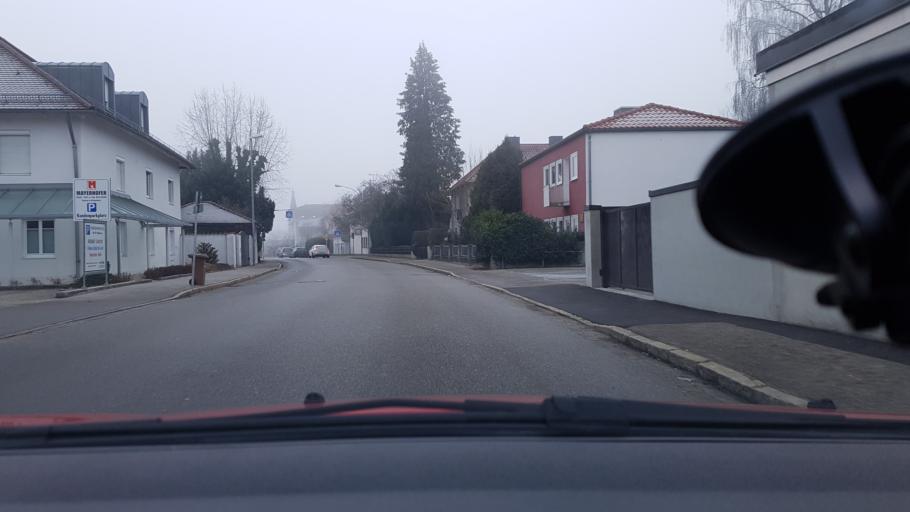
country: DE
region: Bavaria
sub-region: Lower Bavaria
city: Simbach am Inn
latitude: 48.2673
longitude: 13.0224
